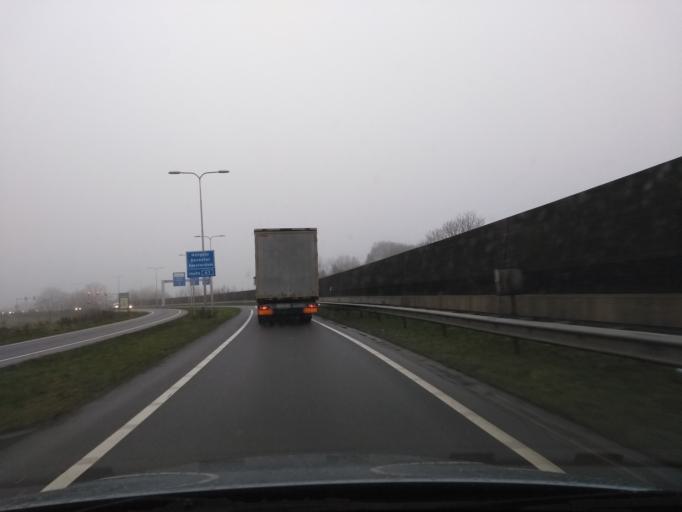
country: NL
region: Overijssel
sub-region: Gemeente Wierden
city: Wierden
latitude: 52.3554
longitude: 6.6122
